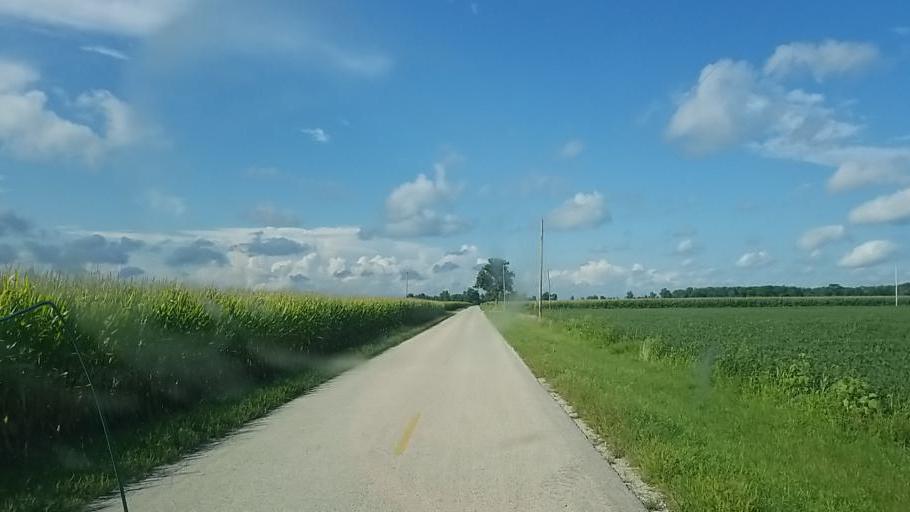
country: US
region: Ohio
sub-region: Hardin County
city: Forest
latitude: 40.7222
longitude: -83.5145
